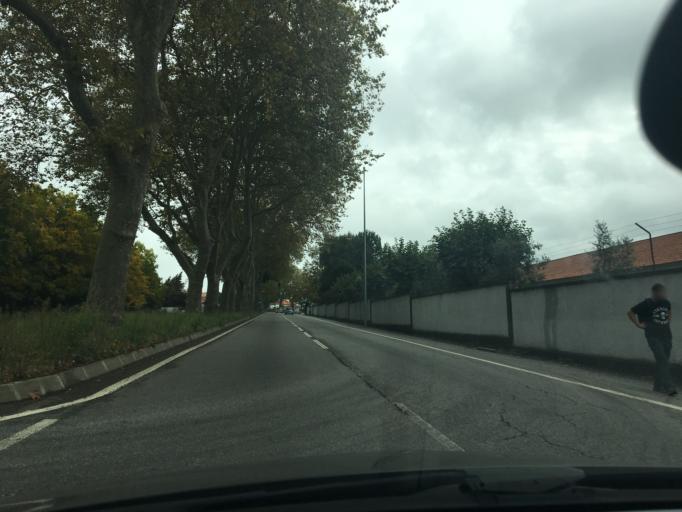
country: PT
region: Porto
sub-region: Matosinhos
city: Senhora da Hora
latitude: 41.1835
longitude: -8.6445
